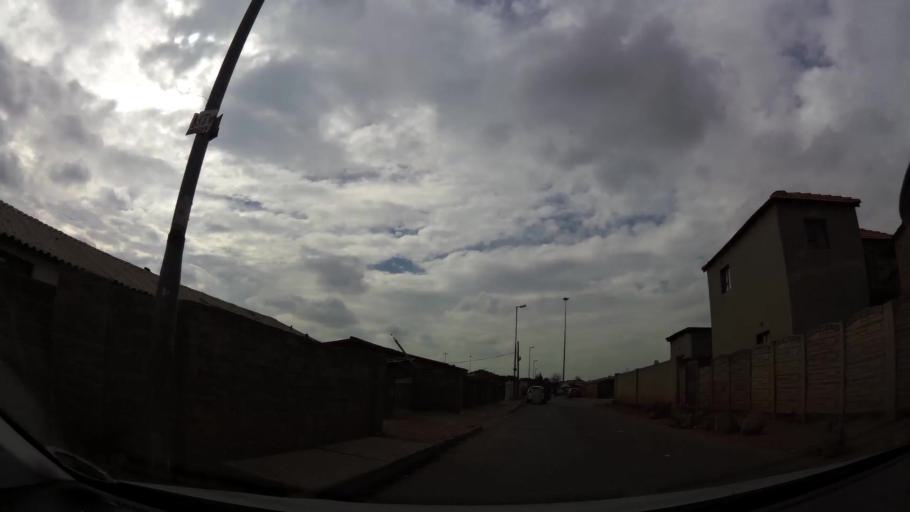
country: ZA
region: Gauteng
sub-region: City of Johannesburg Metropolitan Municipality
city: Soweto
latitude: -26.2742
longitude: 27.8530
